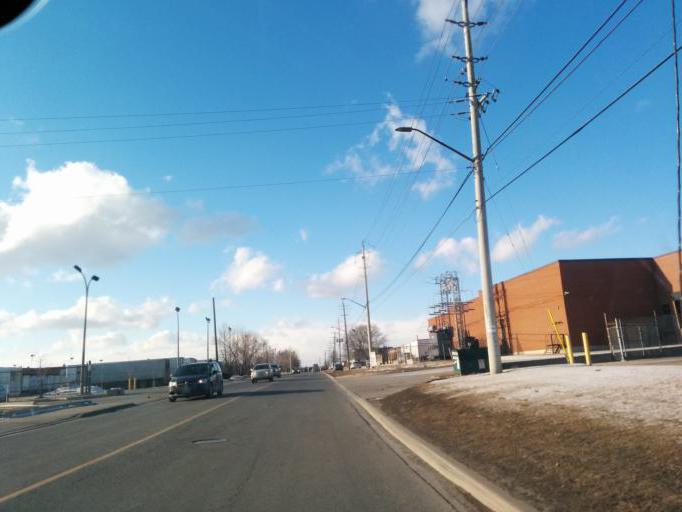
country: CA
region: Ontario
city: Mississauga
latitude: 43.6311
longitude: -79.6285
